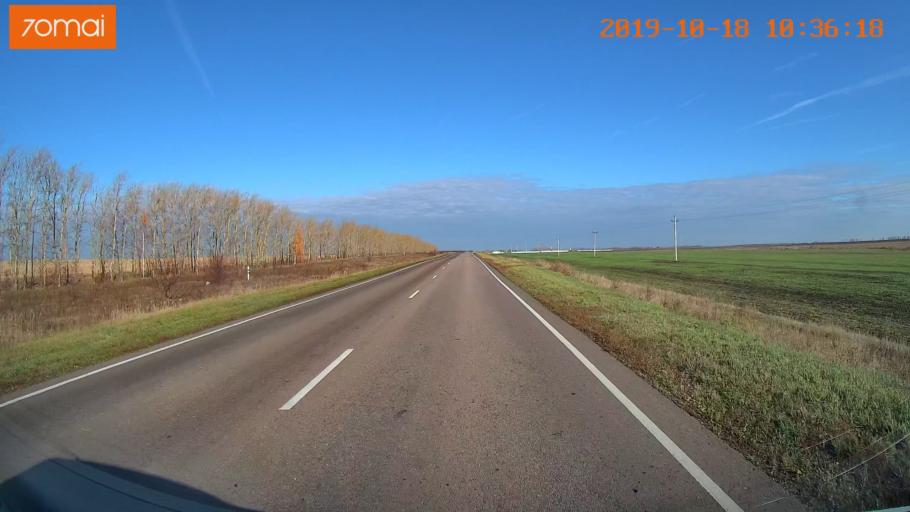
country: RU
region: Tula
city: Kurkino
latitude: 53.5461
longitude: 38.6248
